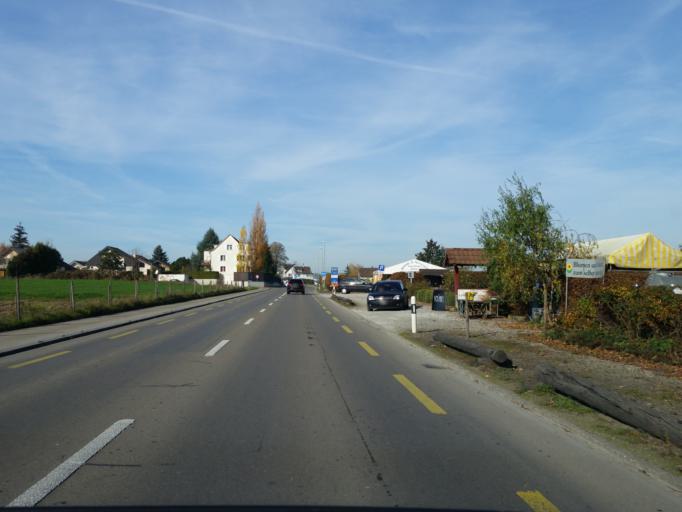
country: CH
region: Thurgau
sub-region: Kreuzlingen District
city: Bottighofen
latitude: 47.6367
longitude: 9.2164
